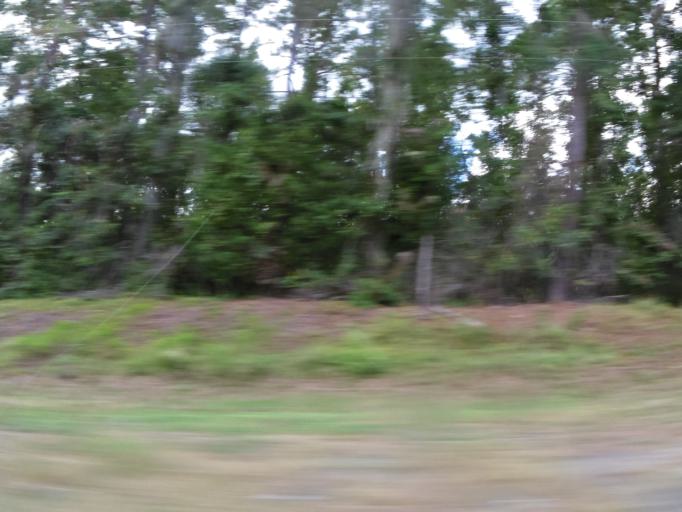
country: US
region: Georgia
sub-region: Liberty County
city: Midway
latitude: 31.8316
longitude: -81.4236
